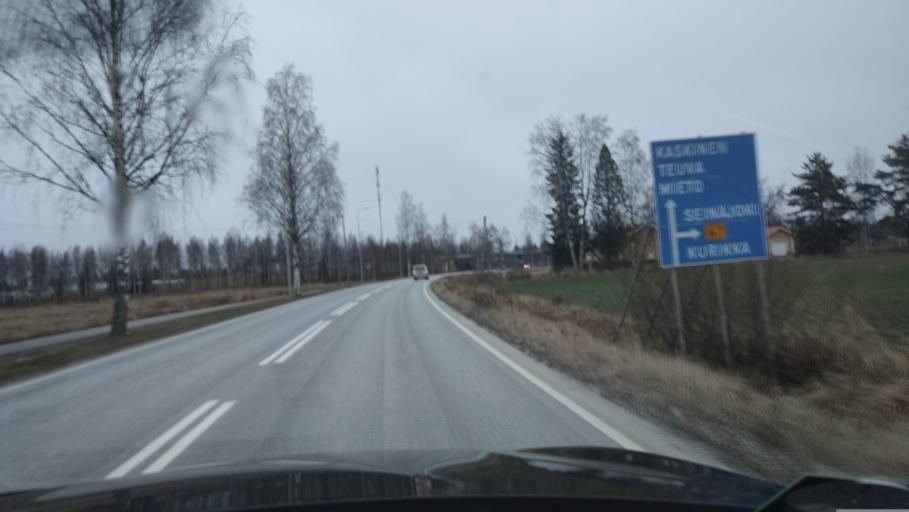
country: FI
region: Southern Ostrobothnia
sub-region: Suupohja
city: Kauhajoki
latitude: 62.4538
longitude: 22.2043
